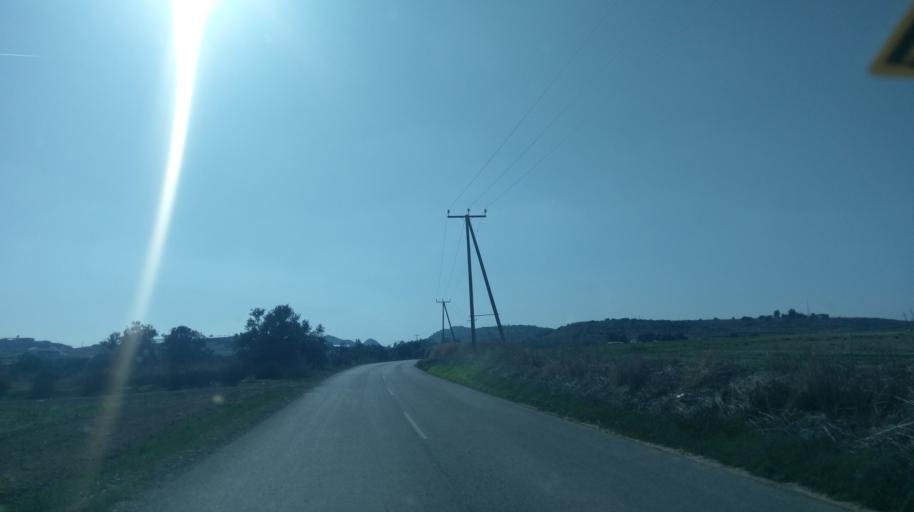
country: CY
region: Lefkosia
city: Lympia
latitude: 35.0260
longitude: 33.4713
